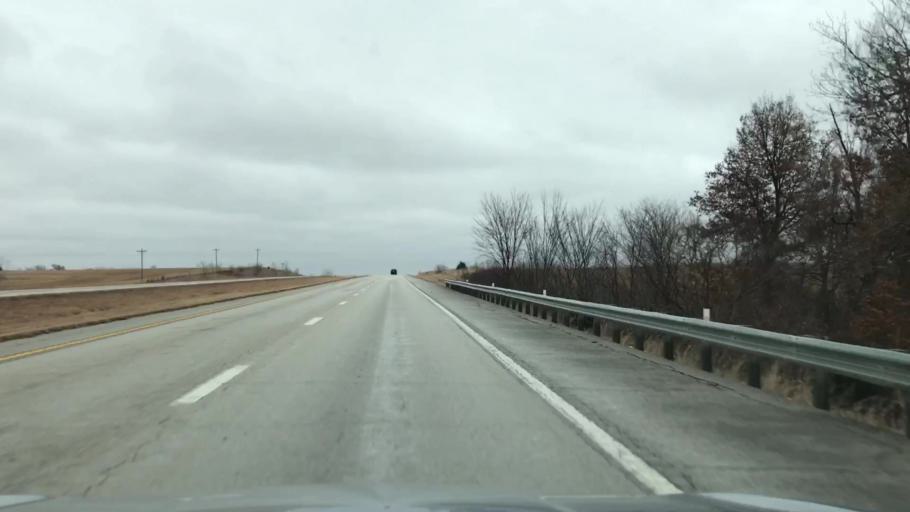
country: US
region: Missouri
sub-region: Clinton County
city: Cameron
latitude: 39.7510
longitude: -94.1443
